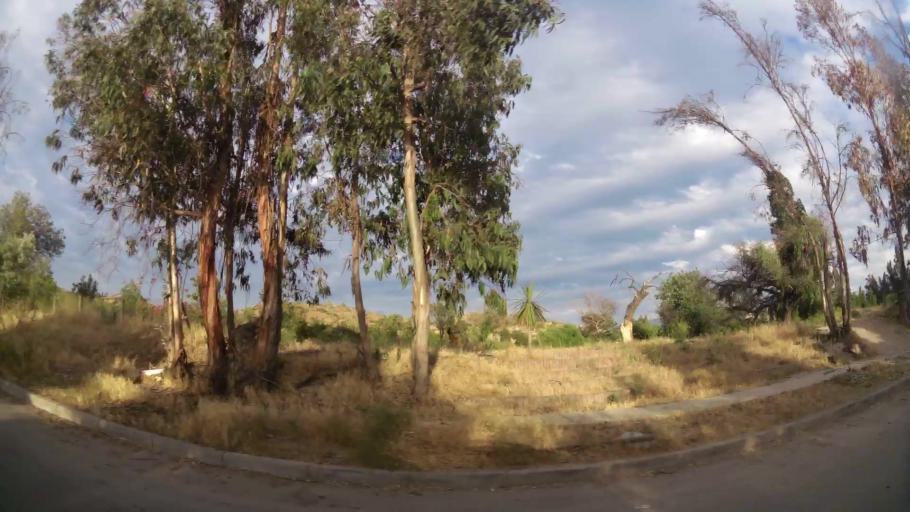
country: CL
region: Santiago Metropolitan
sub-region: Provincia de Maipo
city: San Bernardo
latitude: -33.6366
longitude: -70.6763
